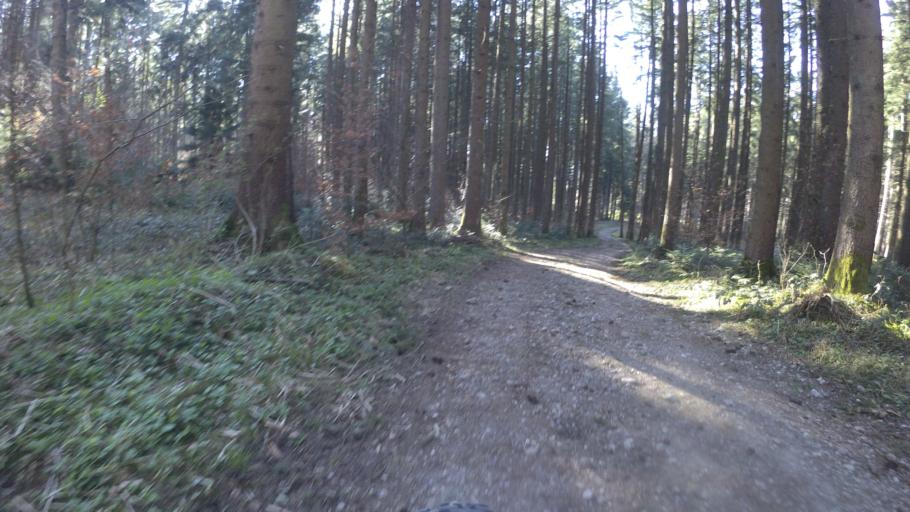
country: DE
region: Bavaria
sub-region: Upper Bavaria
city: Chieming
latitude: 47.9377
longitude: 12.5414
